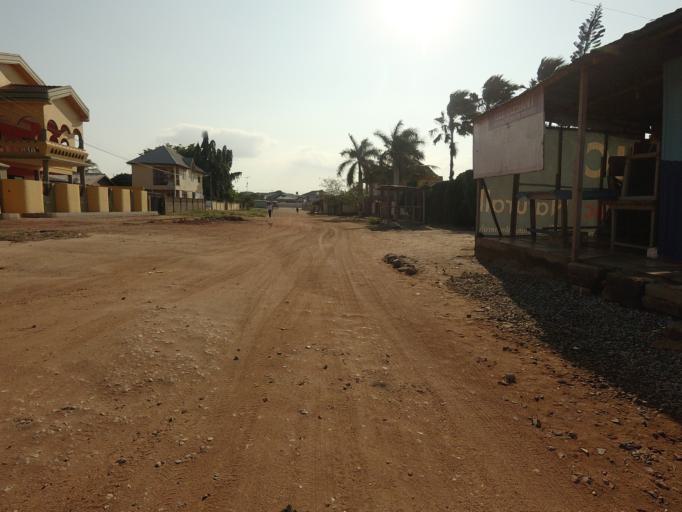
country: GH
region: Greater Accra
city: Nungua
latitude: 5.6362
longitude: -0.0899
